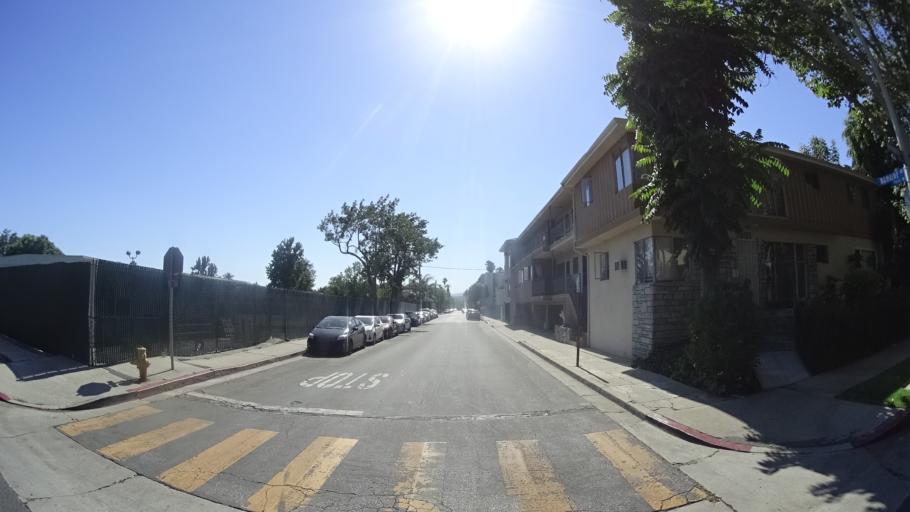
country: US
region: California
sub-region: Los Angeles County
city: West Hollywood
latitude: 34.0888
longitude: -118.3627
